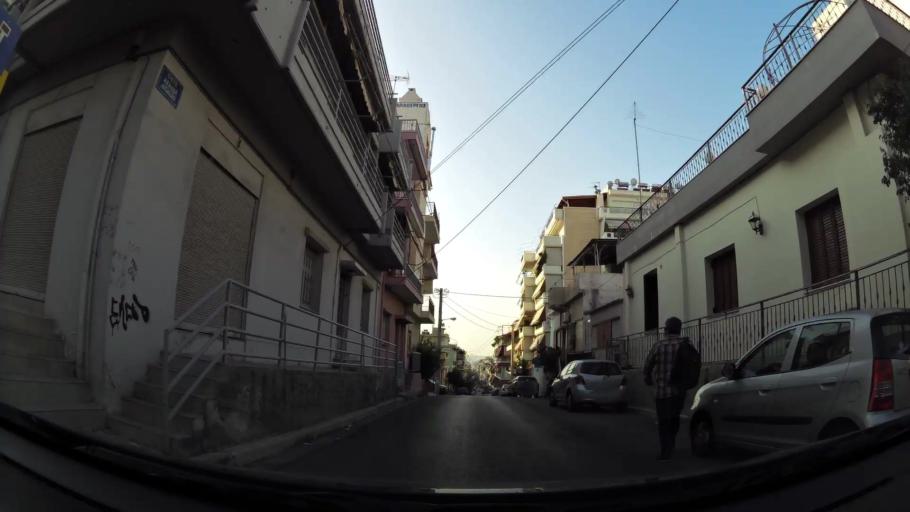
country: GR
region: Attica
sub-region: Nomos Attikis
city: Piraeus
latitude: 37.9594
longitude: 23.6386
